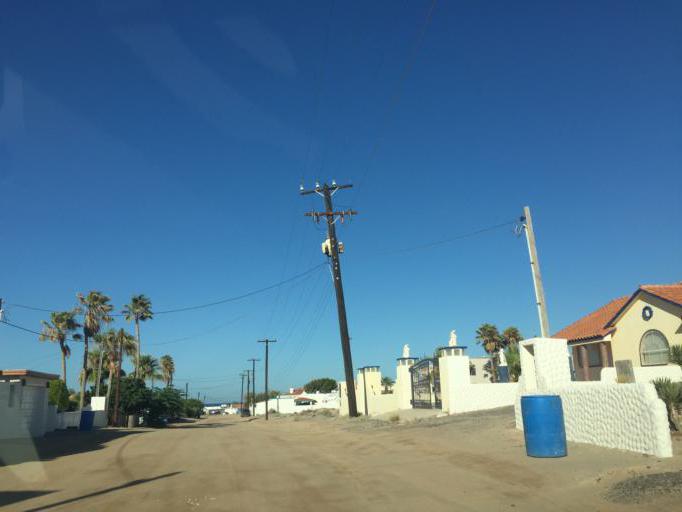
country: MX
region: Sonora
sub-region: Puerto Penasco
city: Puerto Penasco
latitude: 31.2902
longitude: -113.4870
